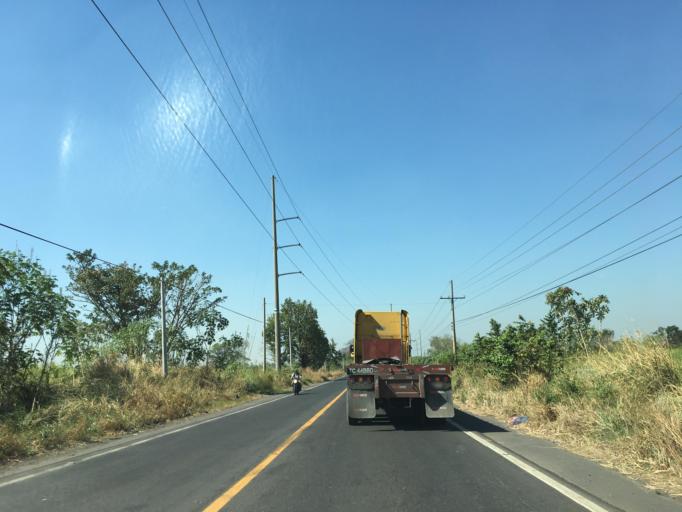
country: GT
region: Escuintla
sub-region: Municipio de Masagua
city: Masagua
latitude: 14.2467
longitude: -90.8092
